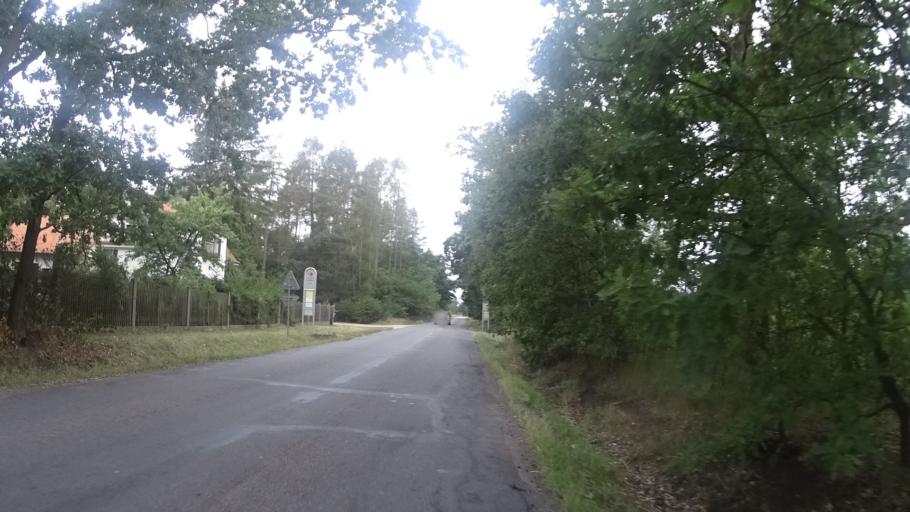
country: CZ
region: Kralovehradecky
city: Cernilov
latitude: 50.2055
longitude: 15.9267
